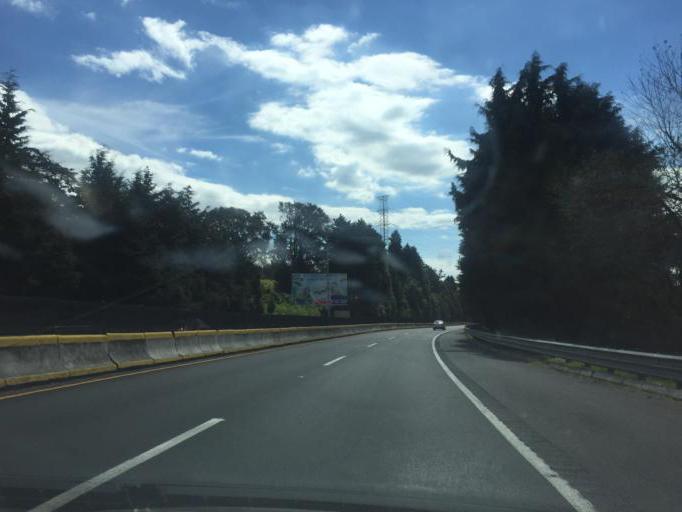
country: MX
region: Morelos
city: Tres Marias
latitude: 19.0474
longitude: -99.2376
